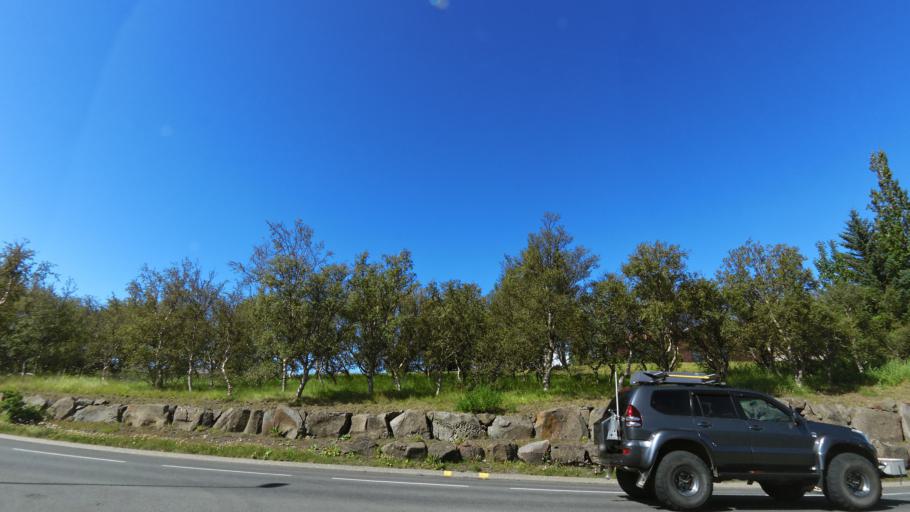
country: IS
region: Capital Region
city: Mosfellsbaer
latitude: 64.1672
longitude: -21.6786
